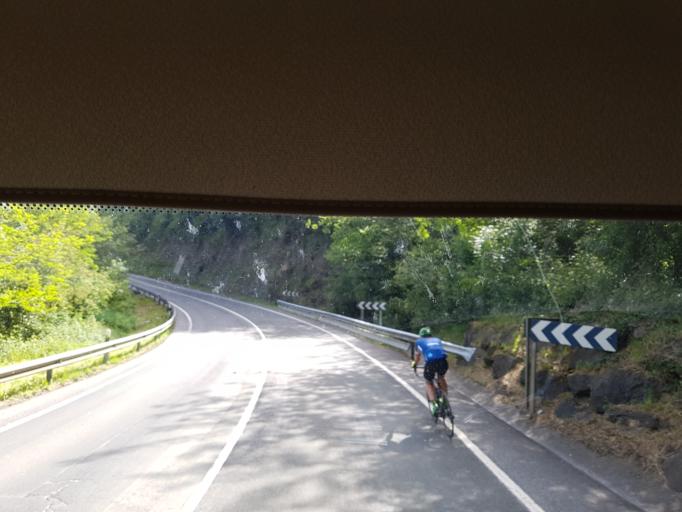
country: ES
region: Basque Country
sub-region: Bizkaia
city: Sopuerta
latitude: 43.2886
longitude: -3.1343
